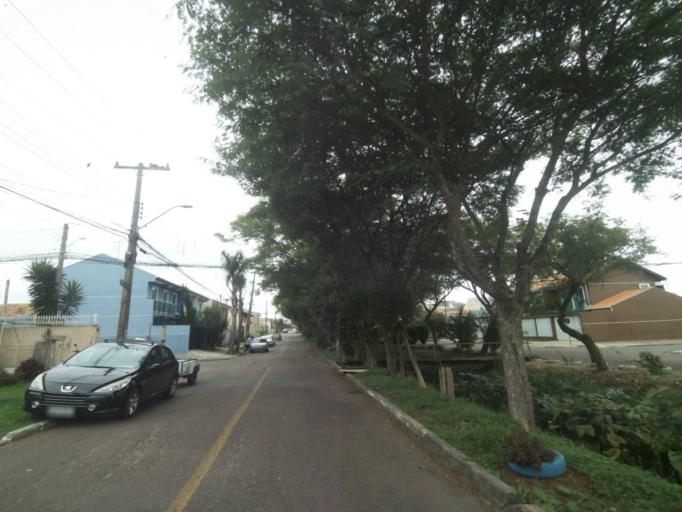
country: BR
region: Parana
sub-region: Araucaria
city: Araucaria
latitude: -25.5493
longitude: -49.3412
